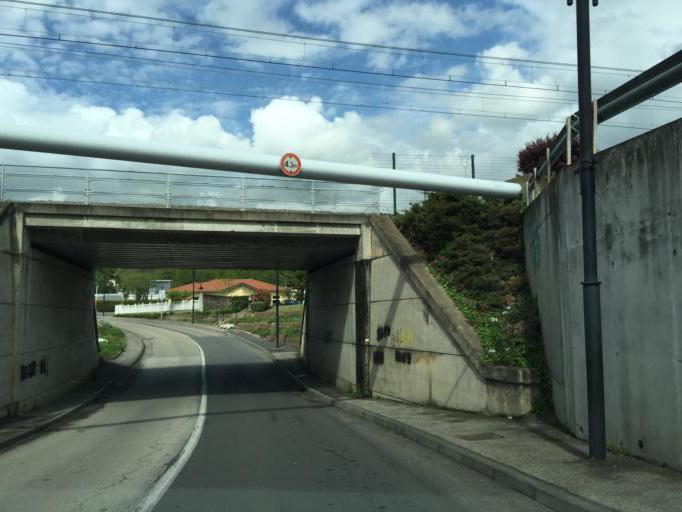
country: FR
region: Rhone-Alpes
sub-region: Departement de la Loire
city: Lorette
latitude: 45.5100
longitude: 4.5738
